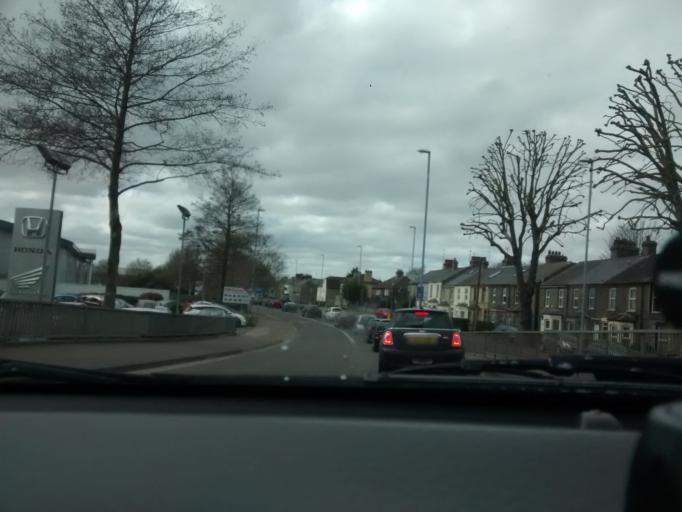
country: GB
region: England
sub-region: Cambridgeshire
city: Cambridge
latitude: 52.2134
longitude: 0.1511
